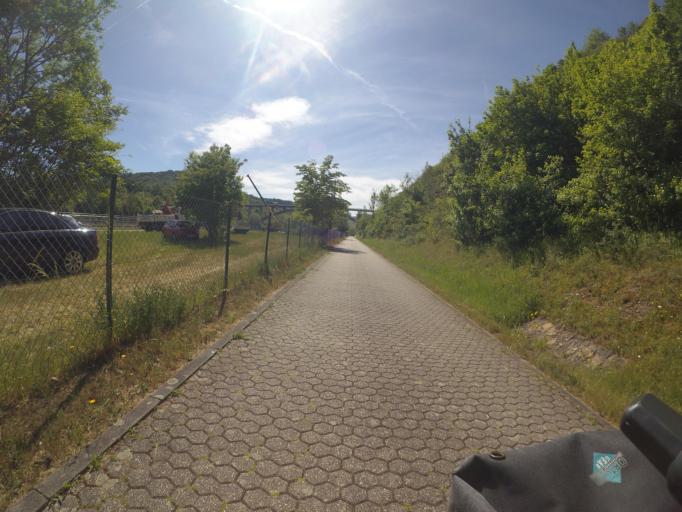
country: DE
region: Rheinland-Pfalz
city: Kanzem
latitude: 49.6583
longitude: 6.5601
